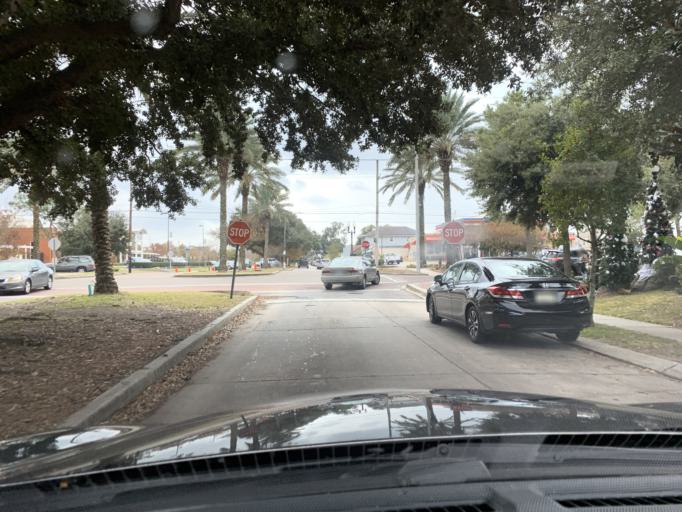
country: US
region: Louisiana
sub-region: Jefferson Parish
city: Metairie
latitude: 30.0046
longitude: -90.1027
